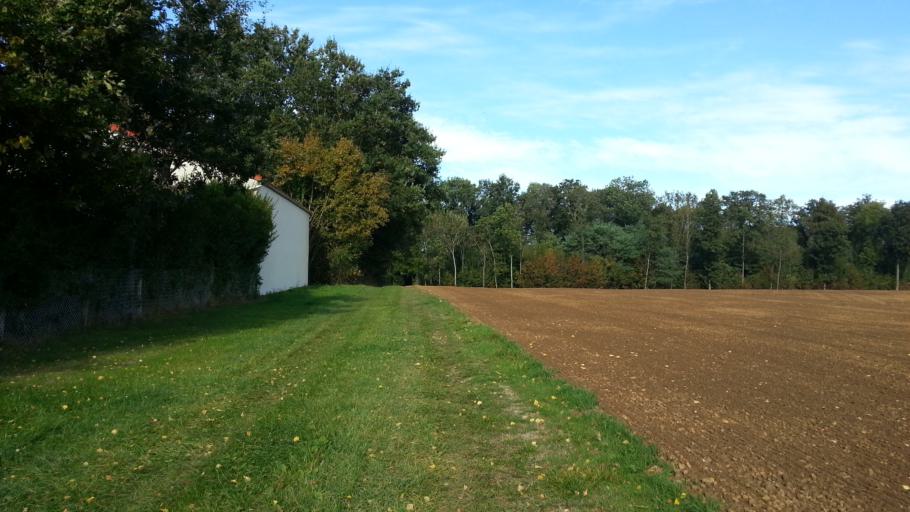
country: FR
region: Ile-de-France
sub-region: Departement de Seine-et-Marne
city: Villiers-Saint-Georges
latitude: 48.7497
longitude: 3.4278
